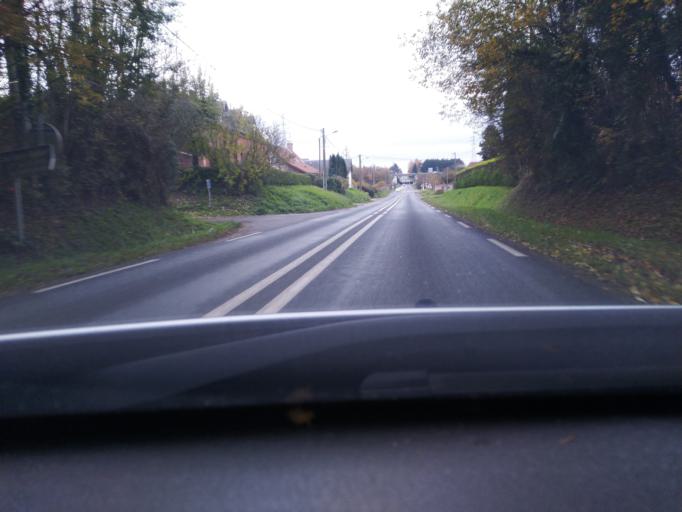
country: FR
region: Haute-Normandie
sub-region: Departement de la Seine-Maritime
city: La Vaupaliere
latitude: 49.4932
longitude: 0.9942
